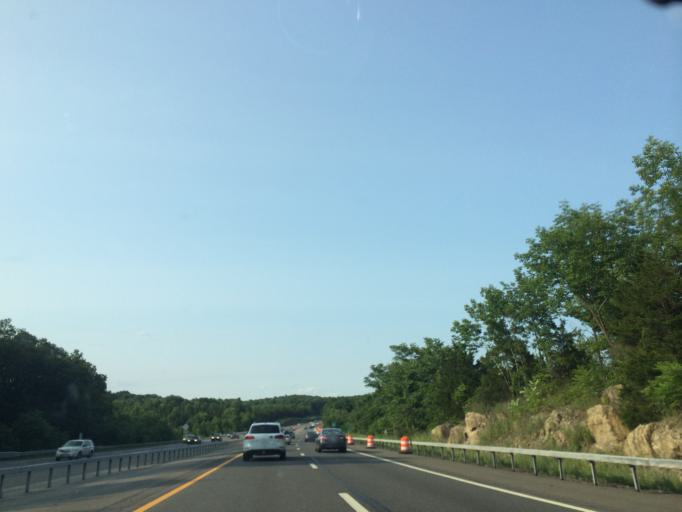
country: US
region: New York
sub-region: Greene County
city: Jefferson Heights
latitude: 42.2153
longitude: -73.9154
